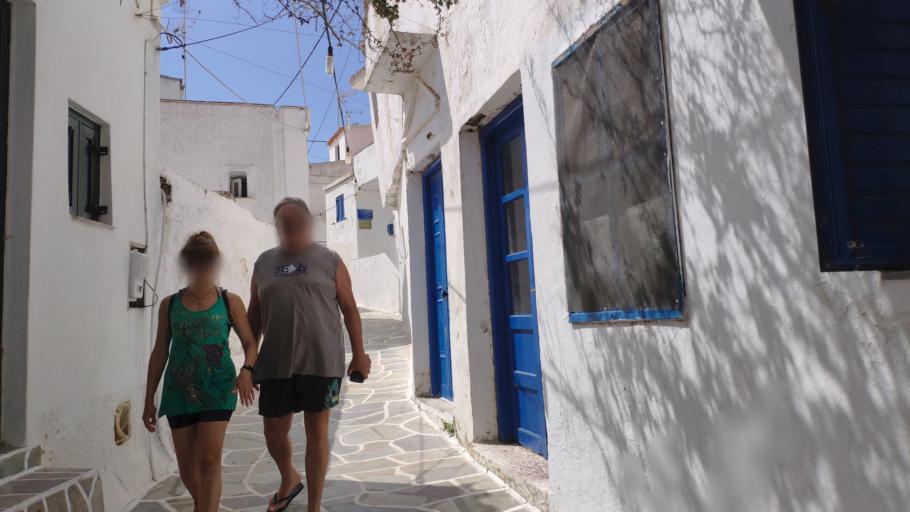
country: GR
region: South Aegean
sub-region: Nomos Kykladon
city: Kythnos
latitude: 37.3824
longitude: 24.4305
